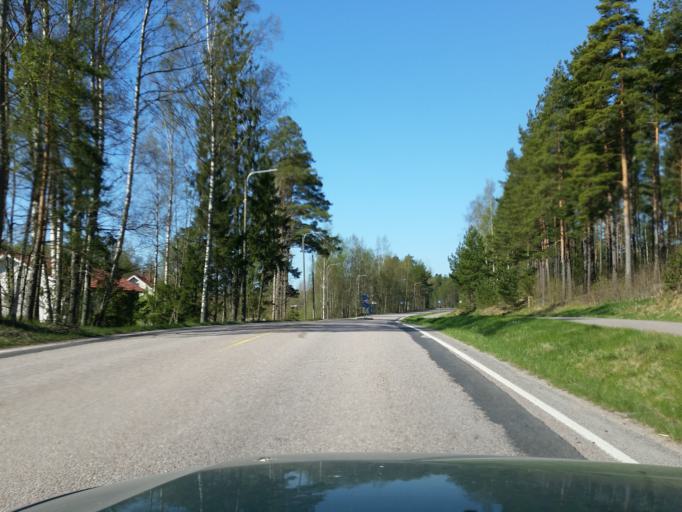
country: FI
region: Uusimaa
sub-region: Helsinki
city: Kirkkonummi
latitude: 60.1309
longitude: 24.4855
